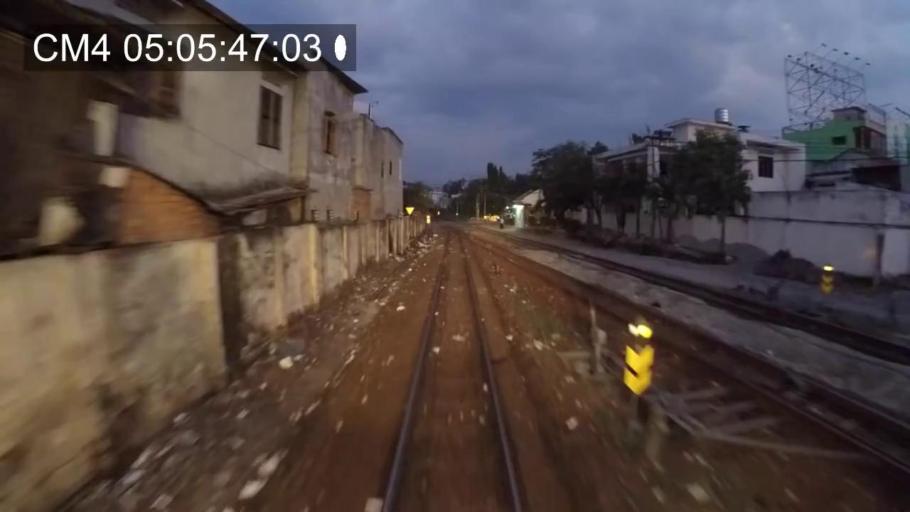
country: VN
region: Khanh Hoa
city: Nha Trang
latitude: 12.2733
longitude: 109.1769
